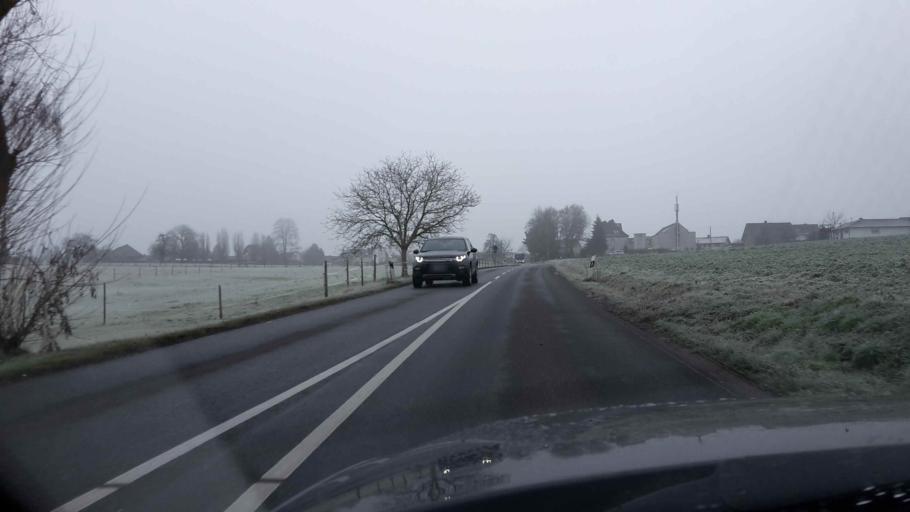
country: DE
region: North Rhine-Westphalia
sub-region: Regierungsbezirk Koln
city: Hennef
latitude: 50.7514
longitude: 7.2741
